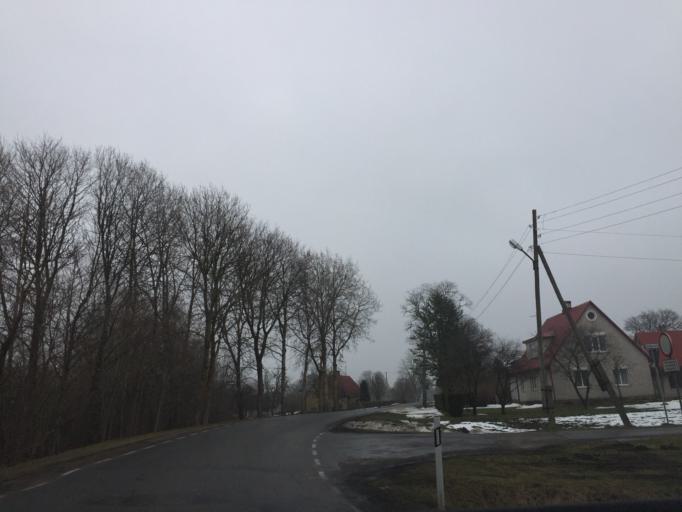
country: EE
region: Saare
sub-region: Orissaare vald
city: Orissaare
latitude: 58.4098
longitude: 22.7938
